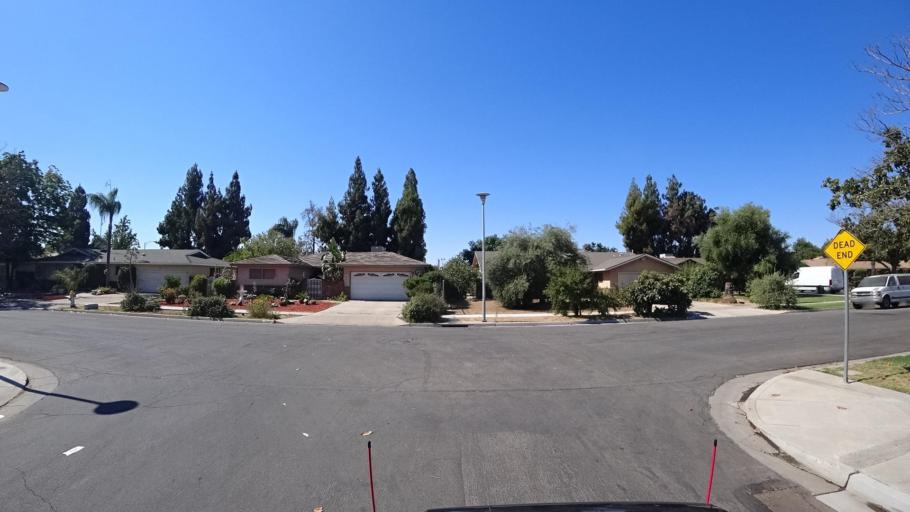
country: US
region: California
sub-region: Fresno County
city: Fresno
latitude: 36.7366
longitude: -119.7758
